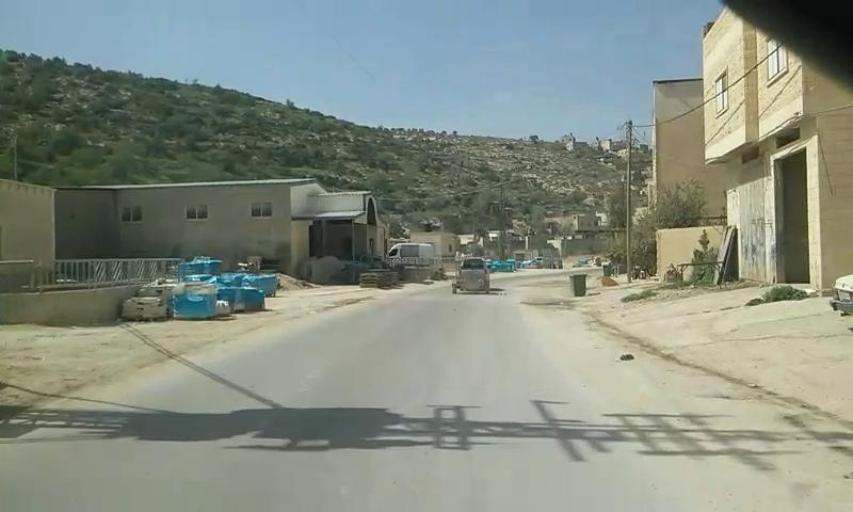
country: PS
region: West Bank
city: Qabatiyah
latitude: 32.4046
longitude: 35.2916
